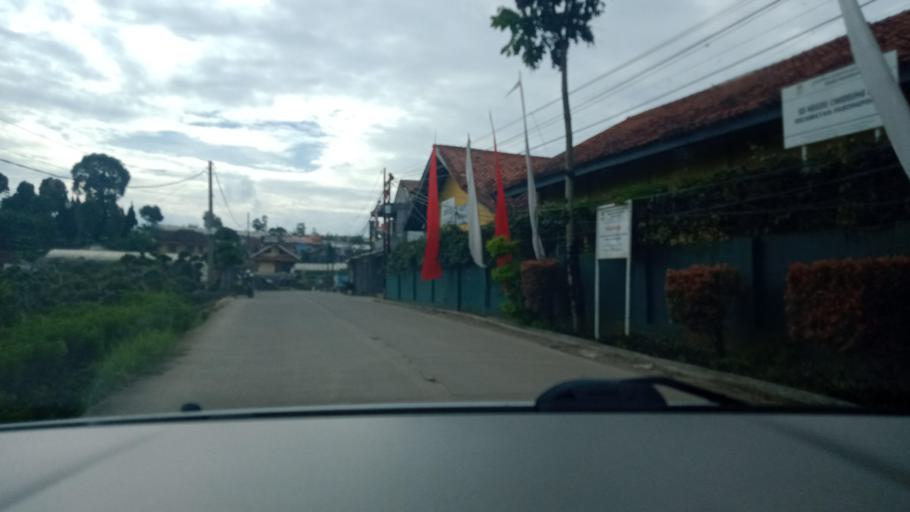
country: ID
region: West Java
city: Lembang
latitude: -6.8117
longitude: 107.5942
